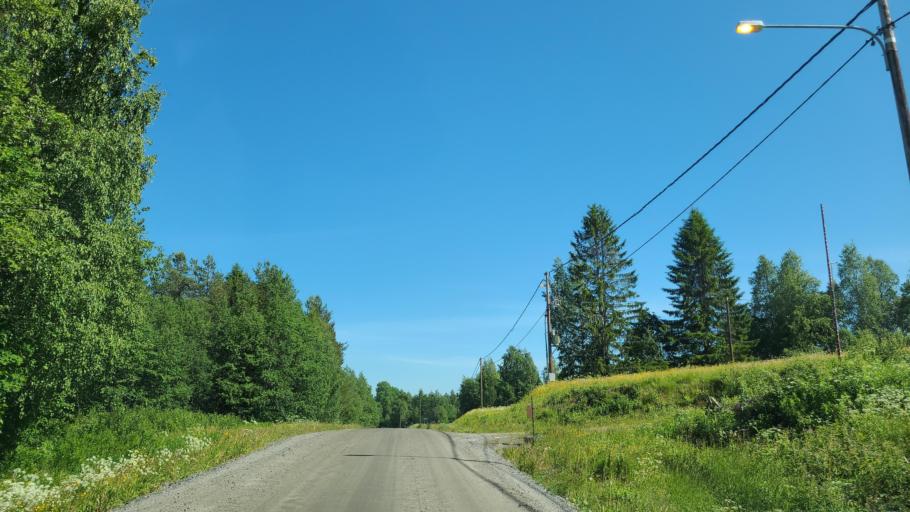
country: SE
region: Vaesterbotten
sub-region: Bjurholms Kommun
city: Bjurholm
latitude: 63.6403
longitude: 19.1782
